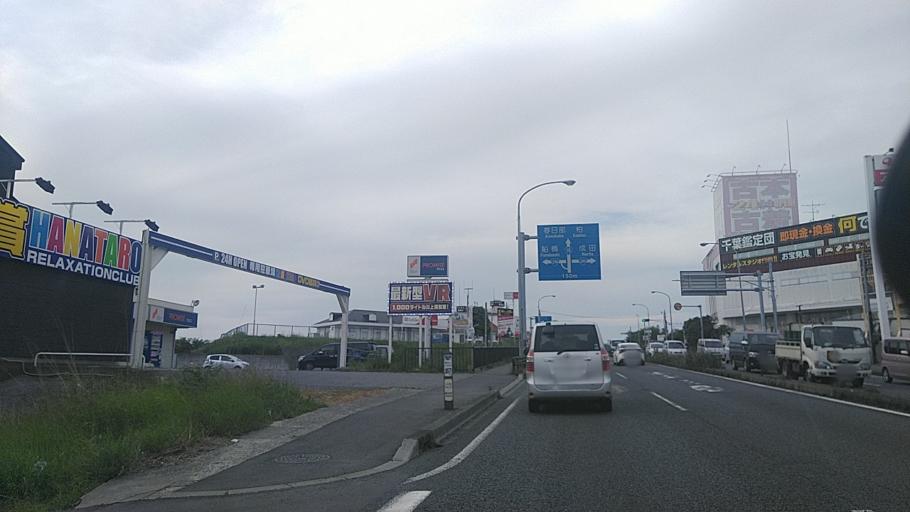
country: JP
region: Chiba
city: Yotsukaido
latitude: 35.7129
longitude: 140.1181
